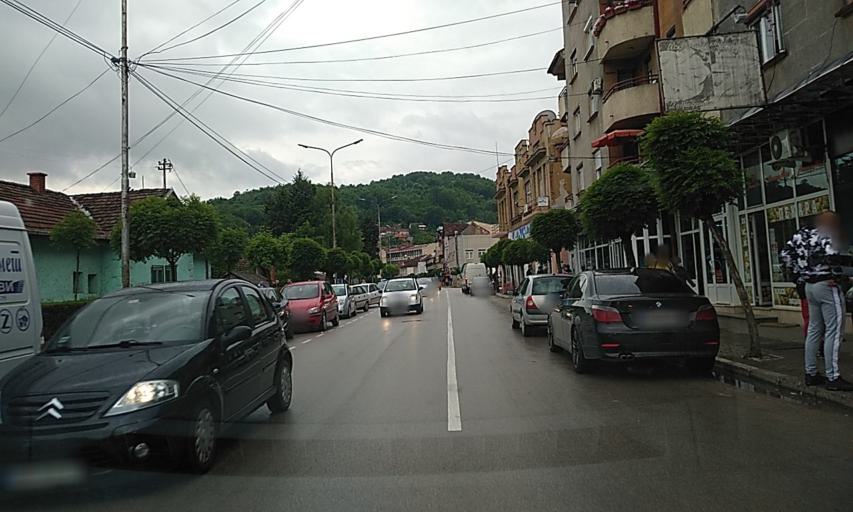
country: RS
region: Central Serbia
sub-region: Pcinjski Okrug
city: Vladicin Han
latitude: 42.7090
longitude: 22.0605
